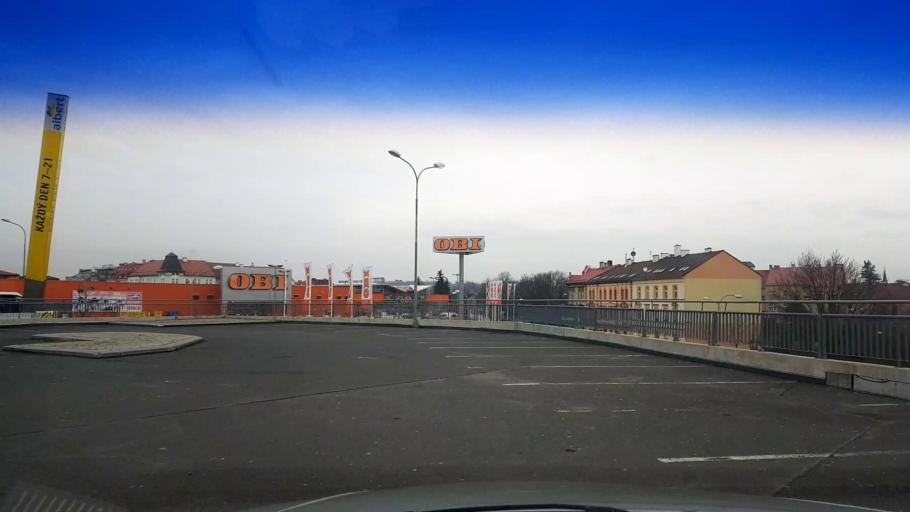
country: CZ
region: Karlovarsky
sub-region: Okres Cheb
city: Cheb
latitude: 50.0717
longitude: 12.3700
